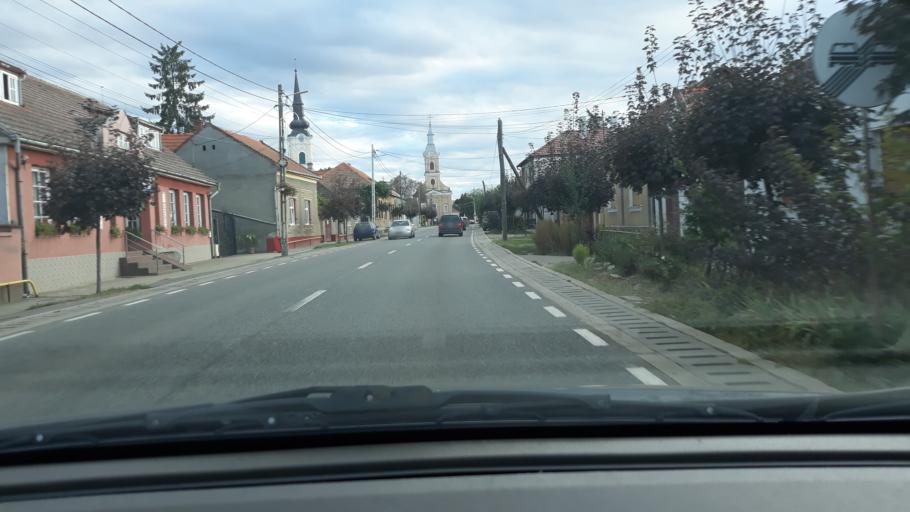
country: RO
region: Bihor
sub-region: Comuna Biharea
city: Biharea
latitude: 47.1551
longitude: 21.9213
